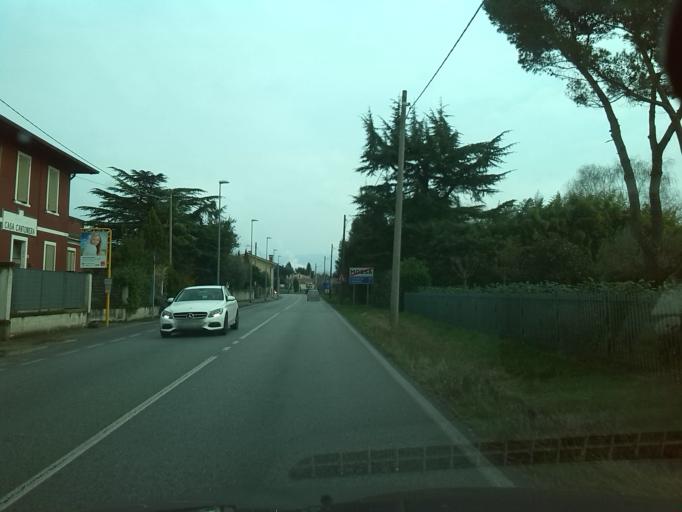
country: IT
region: Friuli Venezia Giulia
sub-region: Provincia di Gorizia
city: Mossa
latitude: 45.9351
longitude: 13.5513
